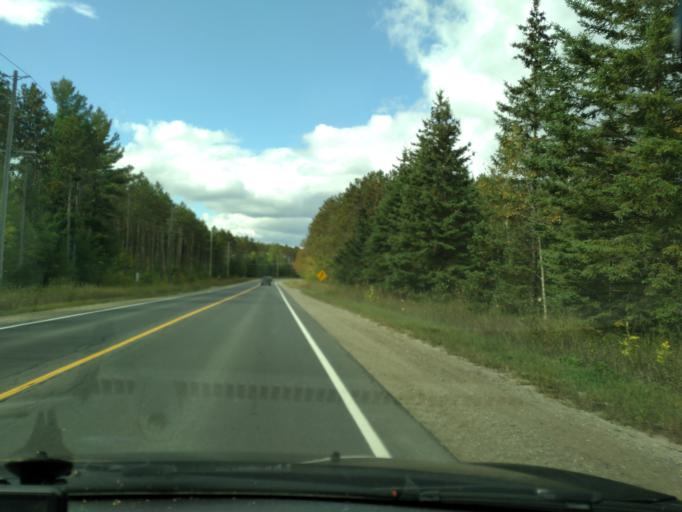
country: CA
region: Ontario
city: Angus
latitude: 44.2530
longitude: -79.8028
